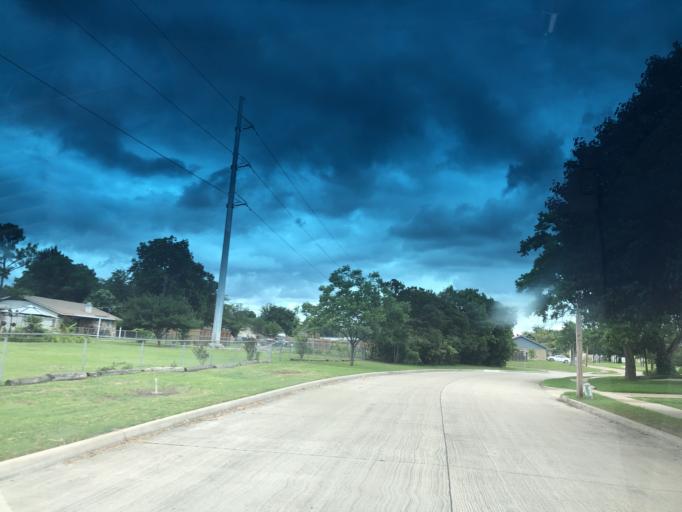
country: US
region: Texas
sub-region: Dallas County
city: Grand Prairie
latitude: 32.7026
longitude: -97.0091
